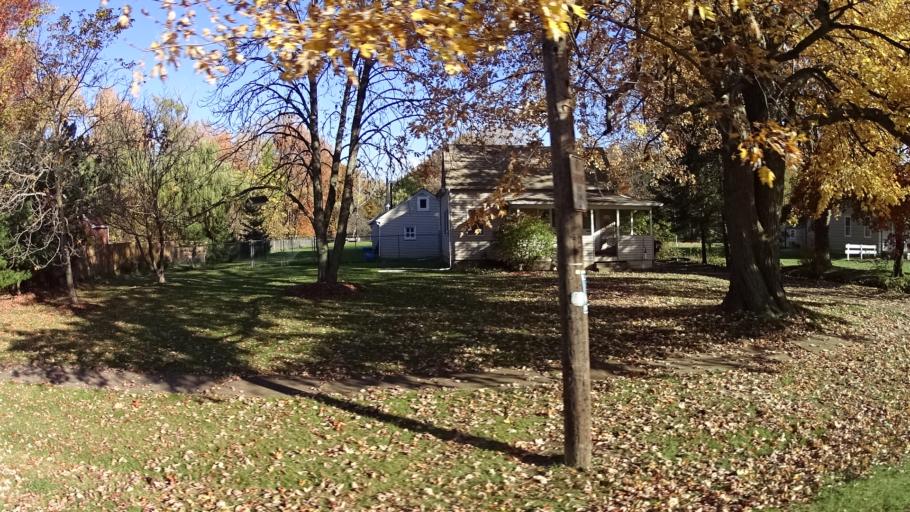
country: US
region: Ohio
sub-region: Lorain County
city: Sheffield Lake
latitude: 41.4724
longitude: -82.1321
